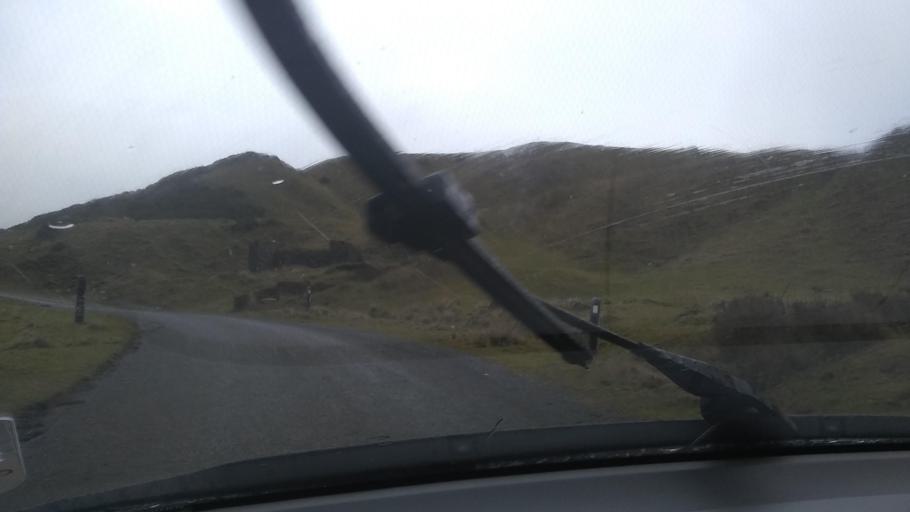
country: GB
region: England
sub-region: Worcestershire
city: Tenbury Wells
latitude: 52.3942
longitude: -2.5967
